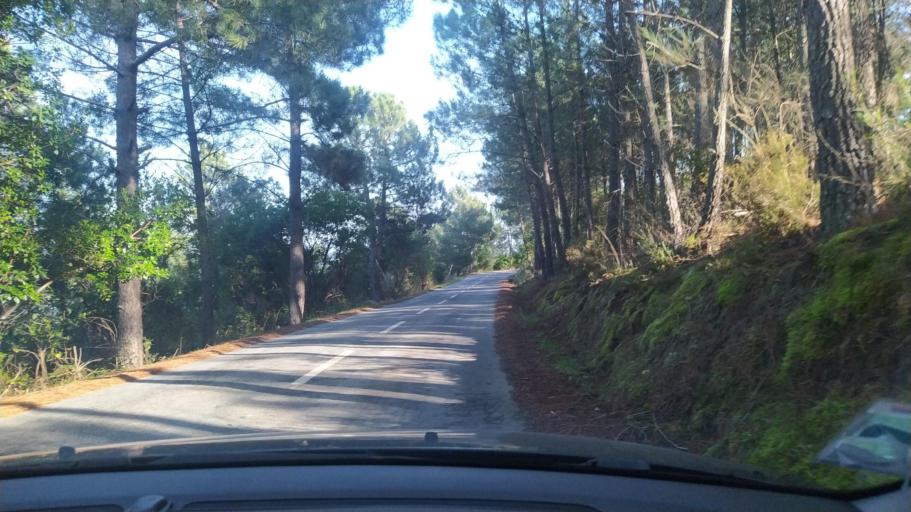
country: PT
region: Castelo Branco
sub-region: Concelho do Fundao
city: Aldeia de Joanes
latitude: 40.1906
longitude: -7.7148
